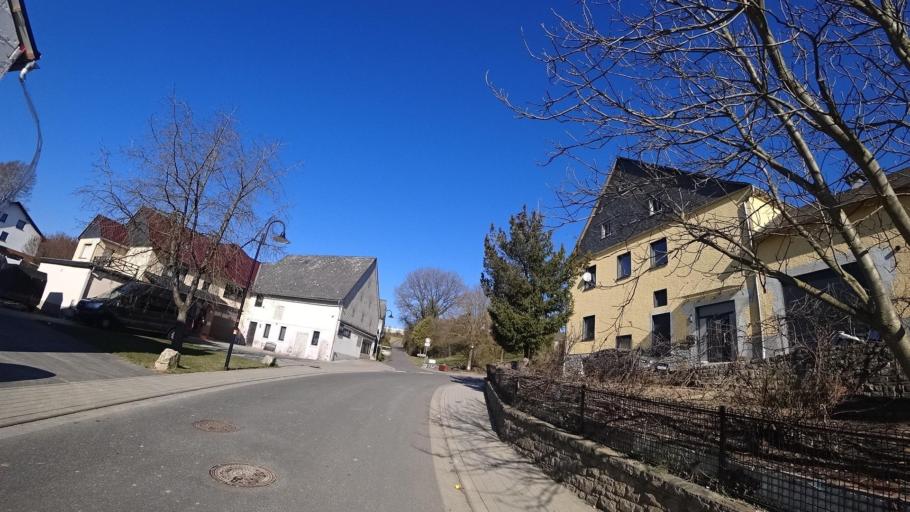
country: DE
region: Rheinland-Pfalz
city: Ohlweiler
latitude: 49.9671
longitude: 7.4957
